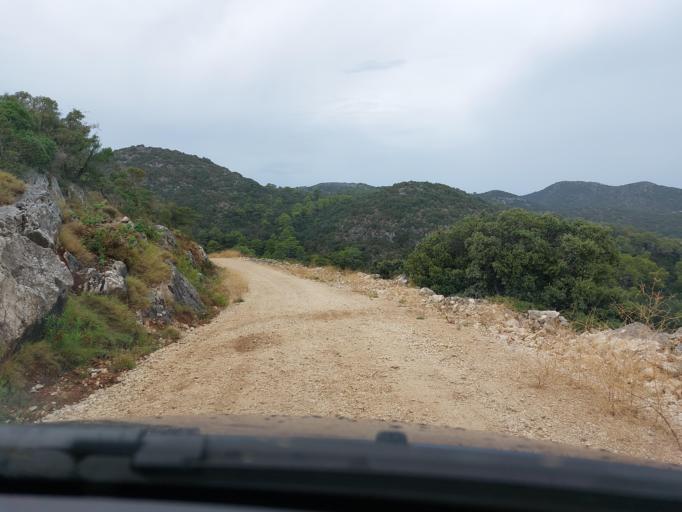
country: HR
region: Dubrovacko-Neretvanska
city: Smokvica
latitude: 42.7480
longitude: 16.9164
